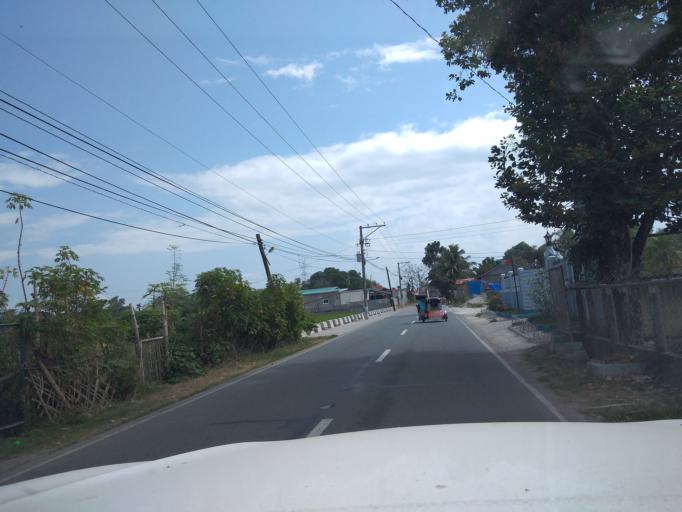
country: PH
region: Central Luzon
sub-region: Province of Pampanga
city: Talang
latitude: 15.0261
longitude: 120.8319
